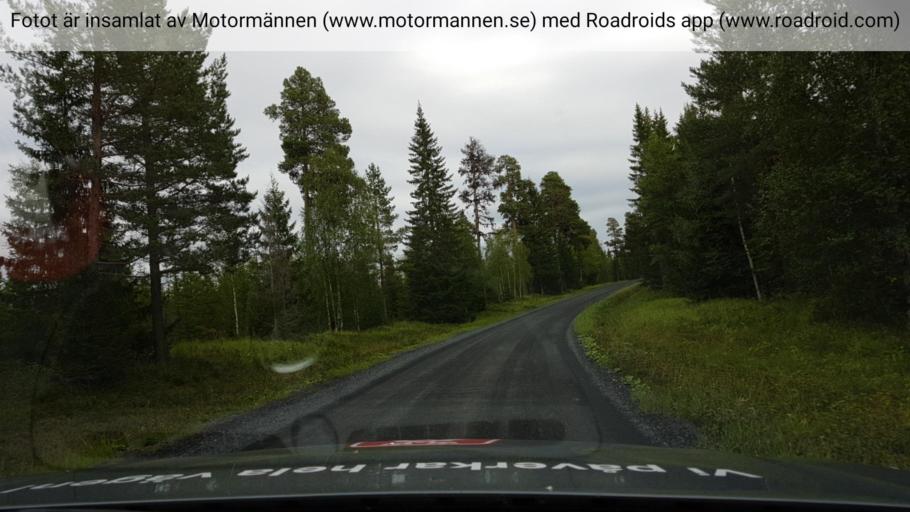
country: SE
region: Jaemtland
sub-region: Krokoms Kommun
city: Valla
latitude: 63.3661
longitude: 13.8922
